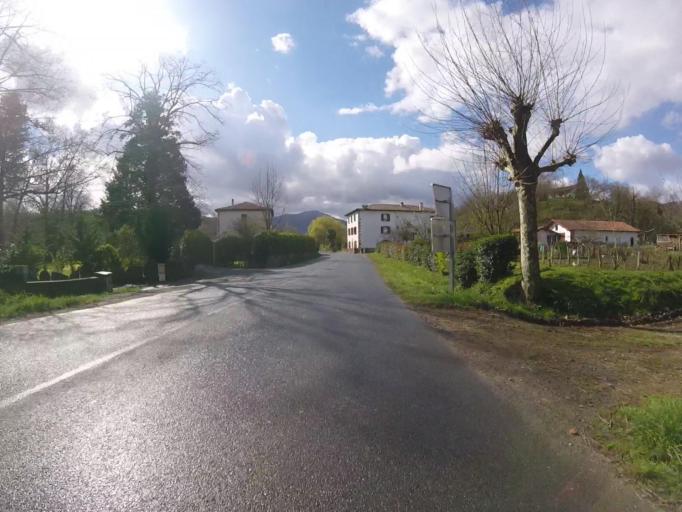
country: FR
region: Aquitaine
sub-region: Departement des Pyrenees-Atlantiques
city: Sare
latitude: 43.3078
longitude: -1.5727
